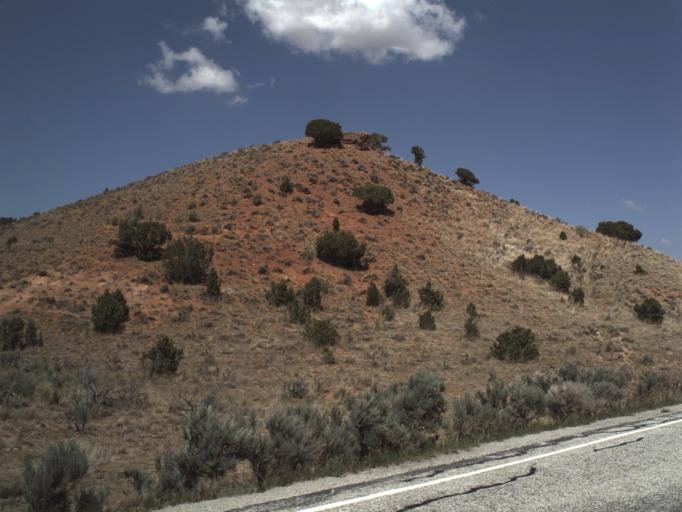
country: US
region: Utah
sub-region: Rich County
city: Randolph
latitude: 41.4976
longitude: -111.2544
